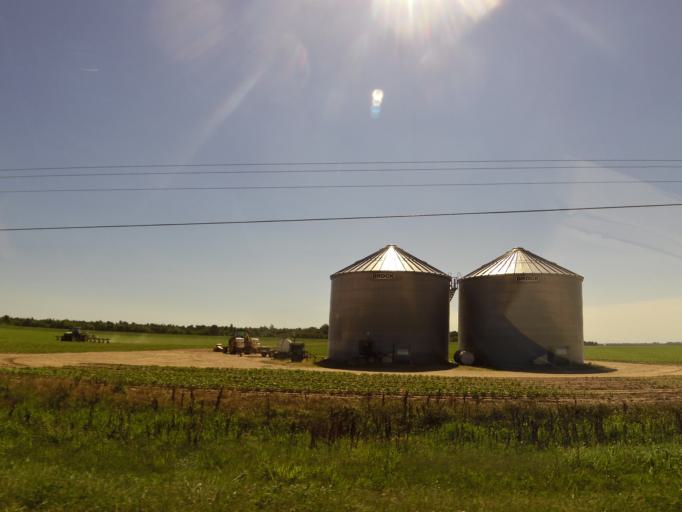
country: US
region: Arkansas
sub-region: Clay County
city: Piggott
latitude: 36.4147
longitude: -90.1475
